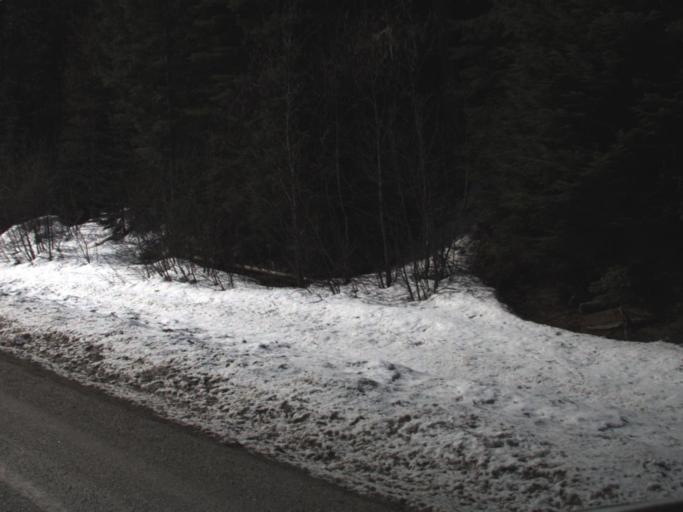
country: US
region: Washington
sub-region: Stevens County
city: Chewelah
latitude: 48.5782
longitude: -117.5576
